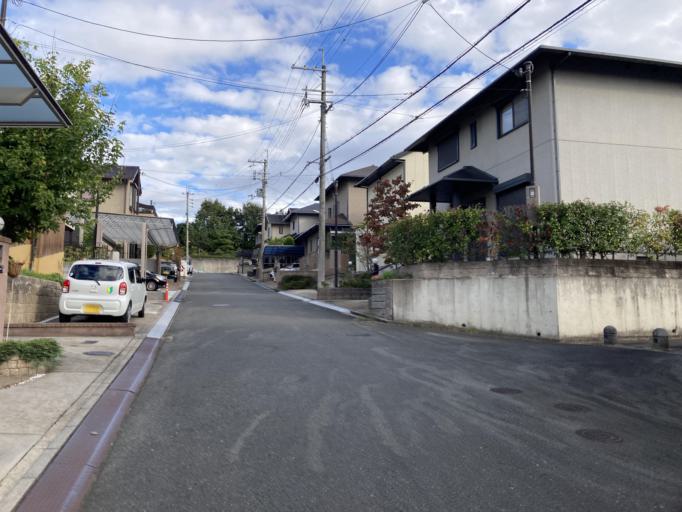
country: JP
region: Nara
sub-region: Ikoma-shi
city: Ikoma
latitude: 34.6787
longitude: 135.7135
